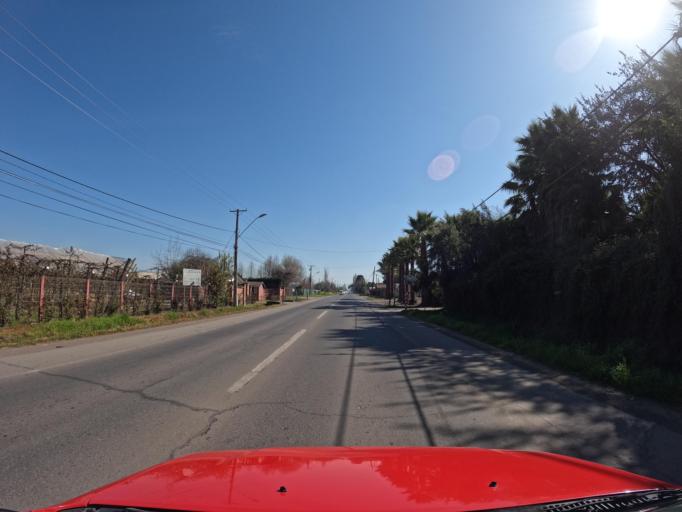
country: CL
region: Maule
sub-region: Provincia de Curico
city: Curico
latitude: -34.9524
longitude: -71.2559
